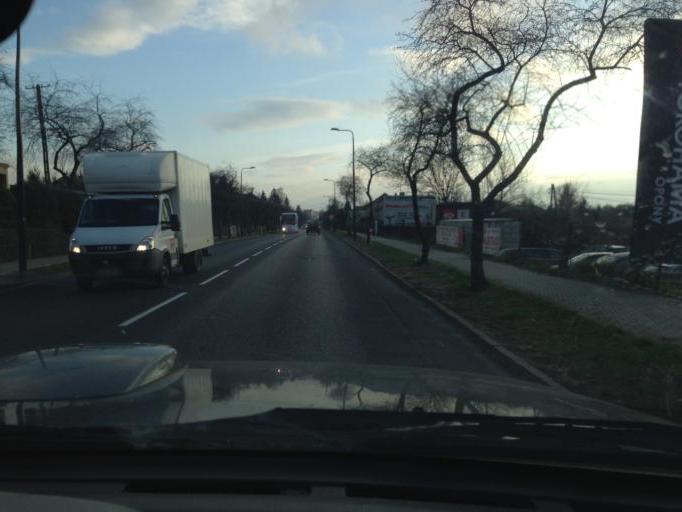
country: PL
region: Subcarpathian Voivodeship
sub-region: Powiat jasielski
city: Jaslo
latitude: 49.7594
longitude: 21.4711
